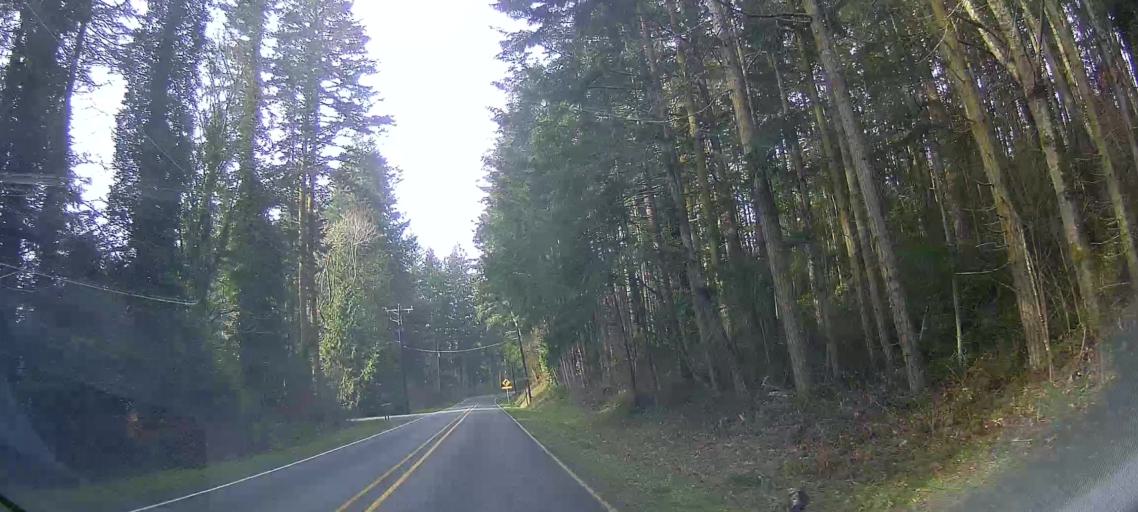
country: US
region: Washington
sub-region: Island County
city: Camano
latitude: 48.1996
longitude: -122.5309
